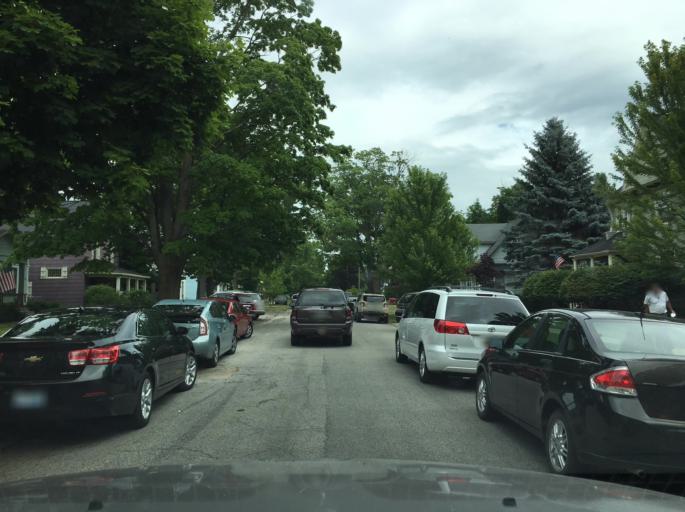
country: US
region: Michigan
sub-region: Mason County
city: Ludington
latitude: 43.9546
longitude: -86.4422
